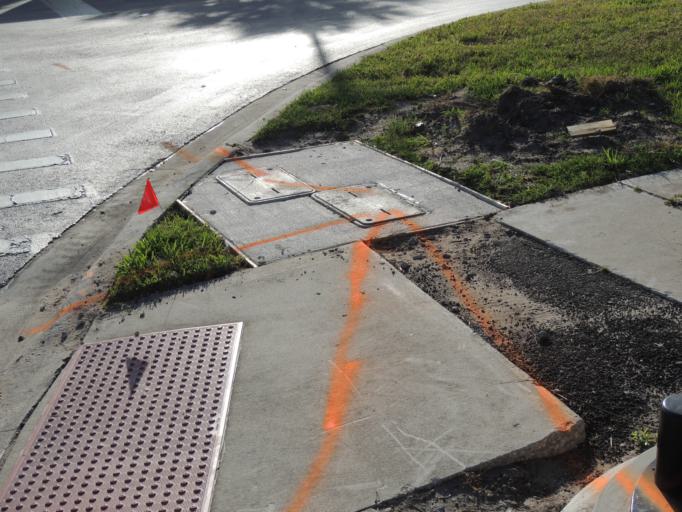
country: US
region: Florida
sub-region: Orange County
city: Hunters Creek
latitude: 28.3400
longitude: -81.3936
